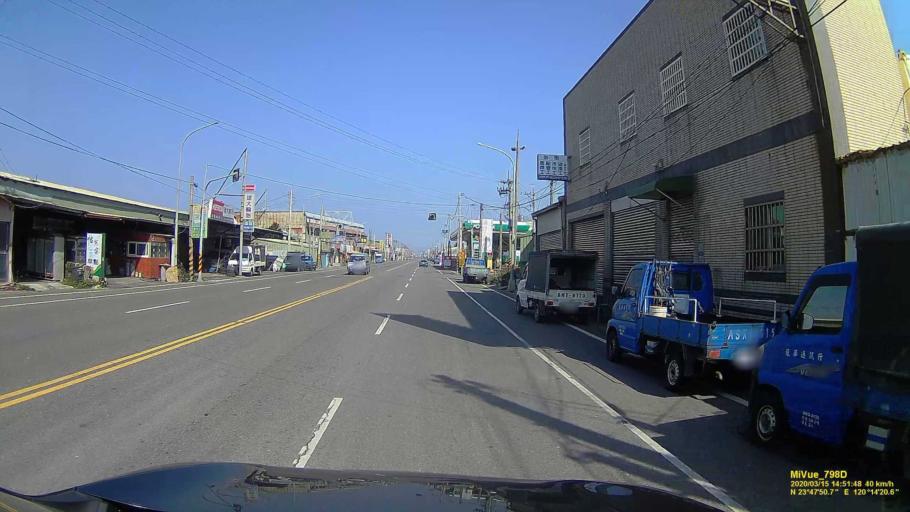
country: TW
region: Taiwan
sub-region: Yunlin
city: Douliu
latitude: 23.7974
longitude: 120.2392
